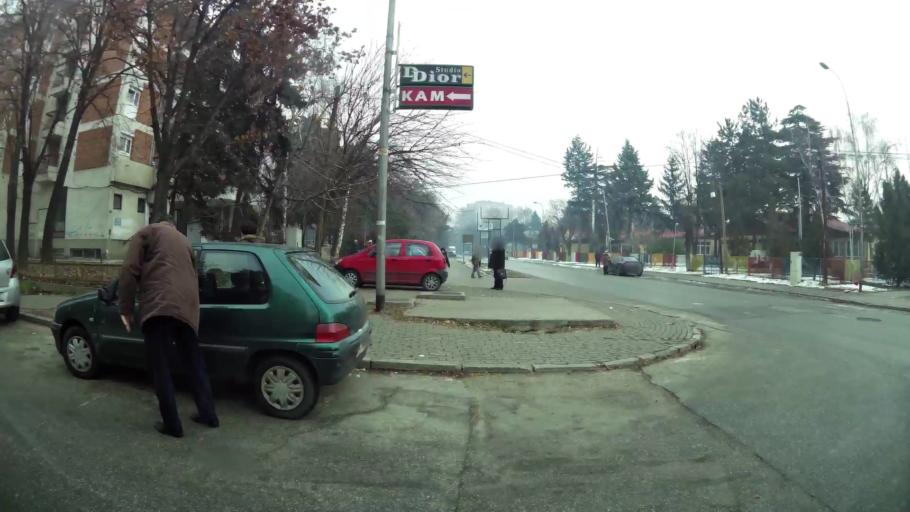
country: MK
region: Cair
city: Cair
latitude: 42.0022
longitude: 21.4623
